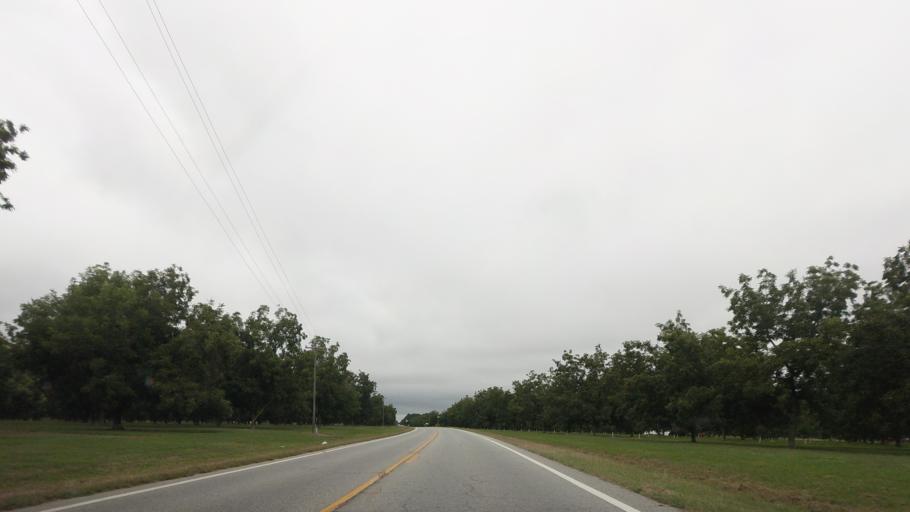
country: US
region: Georgia
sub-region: Berrien County
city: Ray City
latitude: 31.0895
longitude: -83.2056
